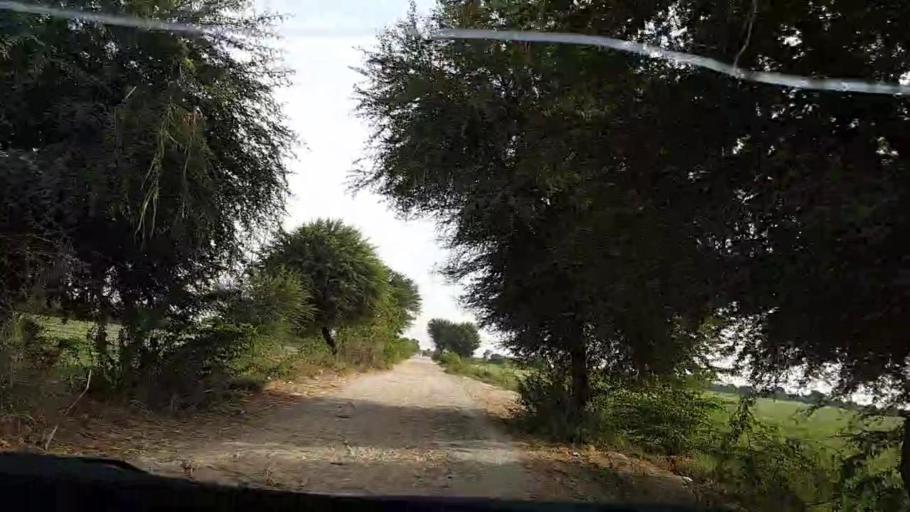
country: PK
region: Sindh
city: Dhoro Naro
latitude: 25.4325
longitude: 69.5220
